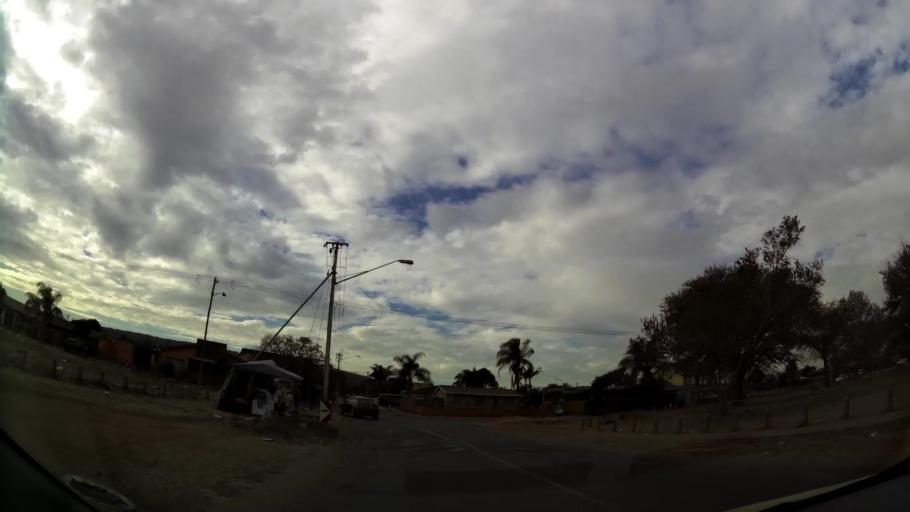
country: ZA
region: Gauteng
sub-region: City of Tshwane Metropolitan Municipality
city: Pretoria
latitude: -25.7104
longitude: 28.3151
